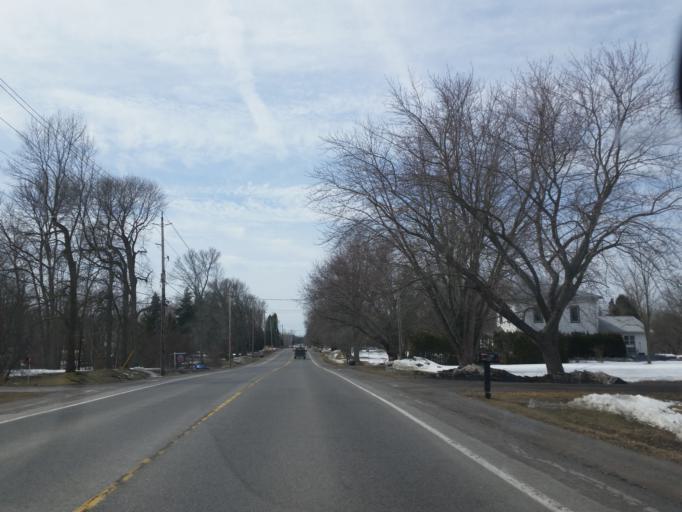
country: CA
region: Ontario
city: Napanee Downtown
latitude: 44.2213
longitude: -76.9787
